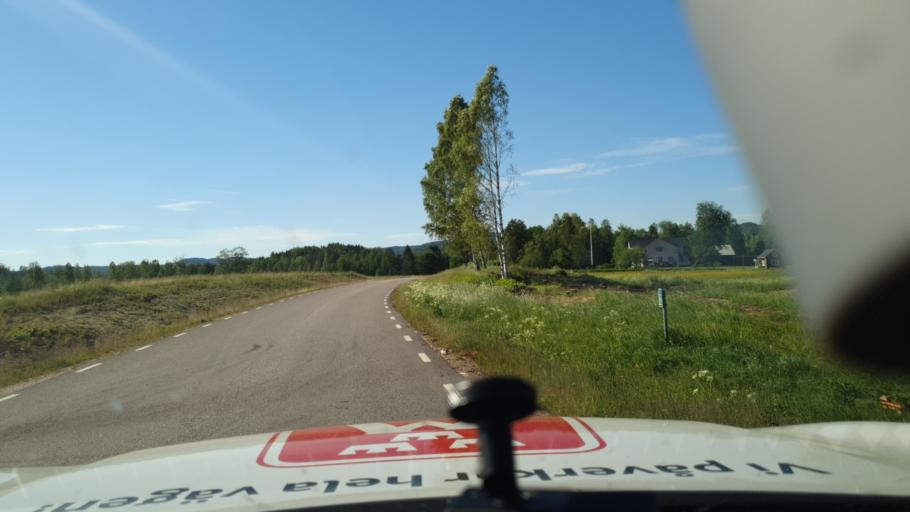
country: SE
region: Vaermland
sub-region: Torsby Kommun
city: Torsby
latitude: 60.2165
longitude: 13.0225
